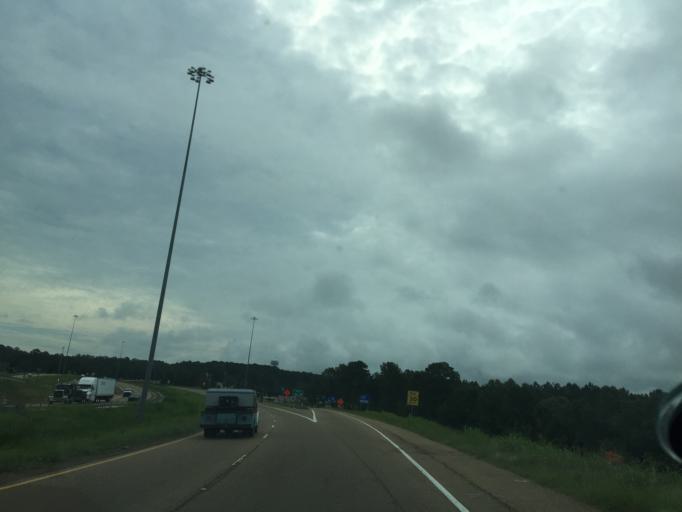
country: US
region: Mississippi
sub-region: Rankin County
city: Brandon
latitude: 32.2781
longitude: -90.0053
